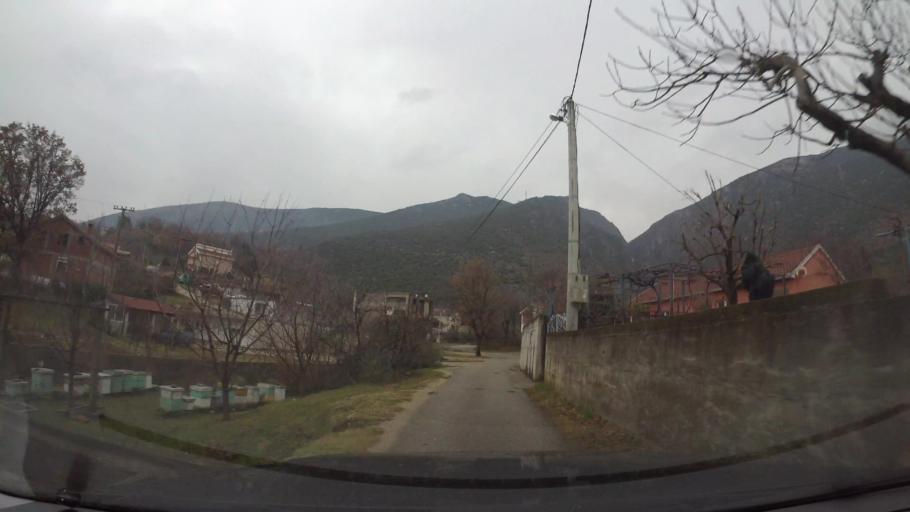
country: BA
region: Federation of Bosnia and Herzegovina
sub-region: Hercegovacko-Bosanski Kanton
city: Mostar
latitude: 43.3678
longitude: 17.8086
